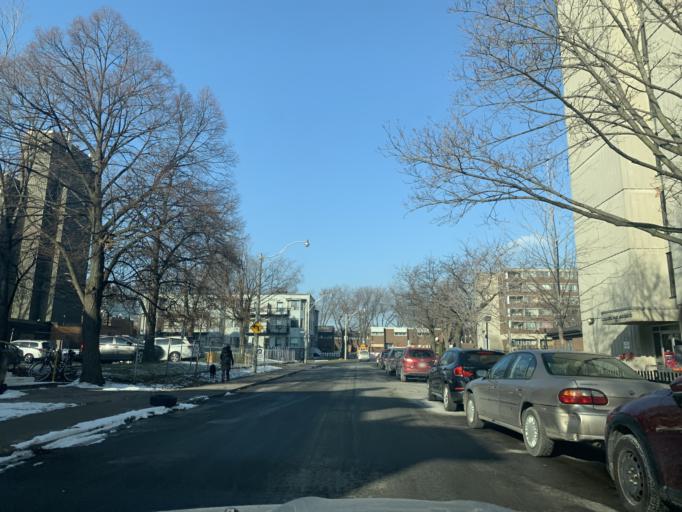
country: CA
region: Ontario
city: Toronto
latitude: 43.6505
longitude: -79.4006
